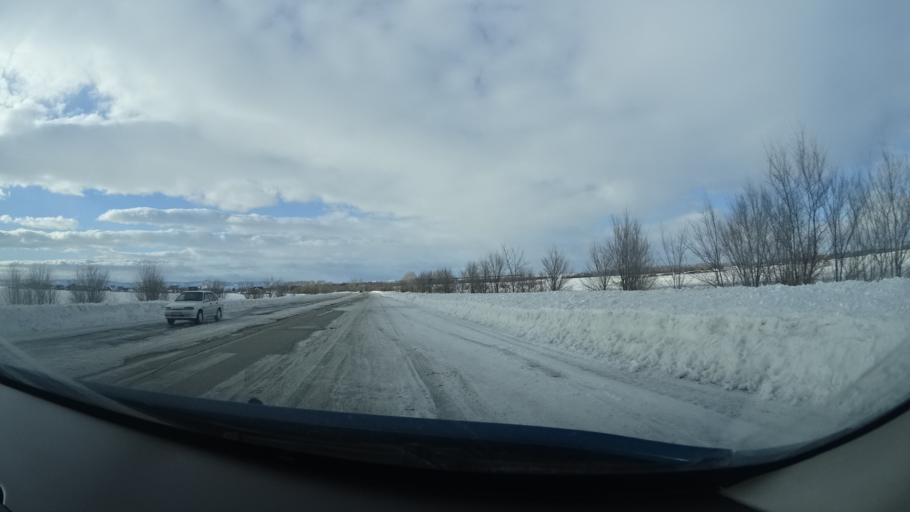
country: RU
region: Chelyabinsk
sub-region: Gorod Magnitogorsk
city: Magnitogorsk
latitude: 53.5881
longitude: 58.8793
